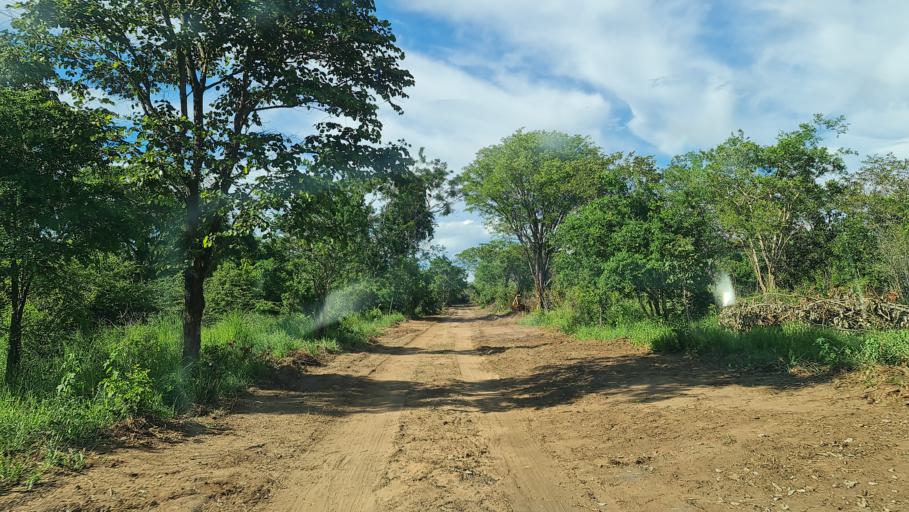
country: MZ
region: Nampula
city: Antonio Enes
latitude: -15.5192
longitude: 40.1291
